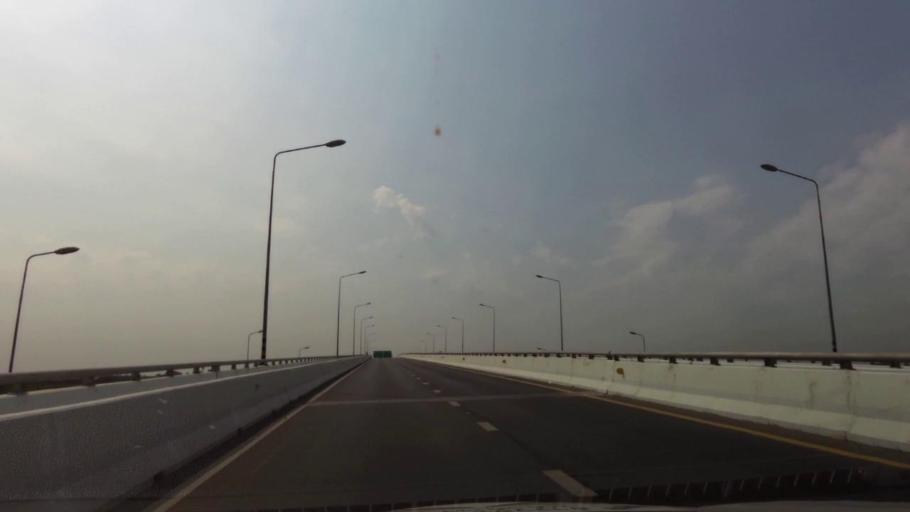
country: TH
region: Phra Nakhon Si Ayutthaya
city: Phra Nakhon Si Ayutthaya
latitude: 14.3303
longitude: 100.5850
